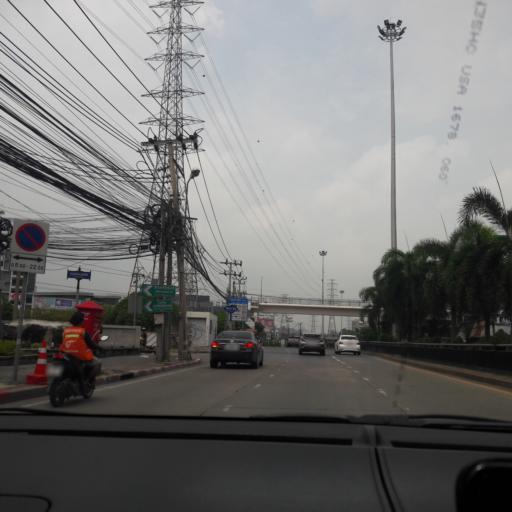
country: TH
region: Bangkok
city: Suan Luang
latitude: 13.7367
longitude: 100.6309
